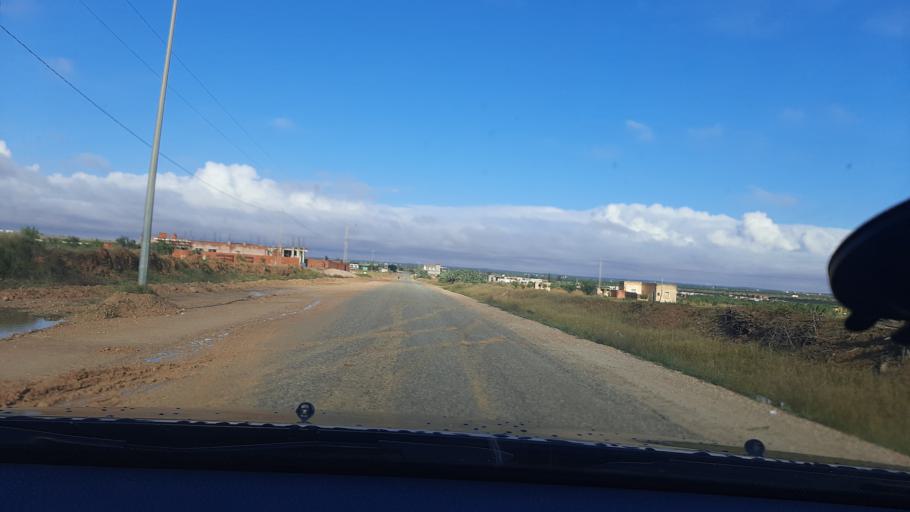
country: TN
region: Safaqis
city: Sfax
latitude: 34.8825
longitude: 10.6306
